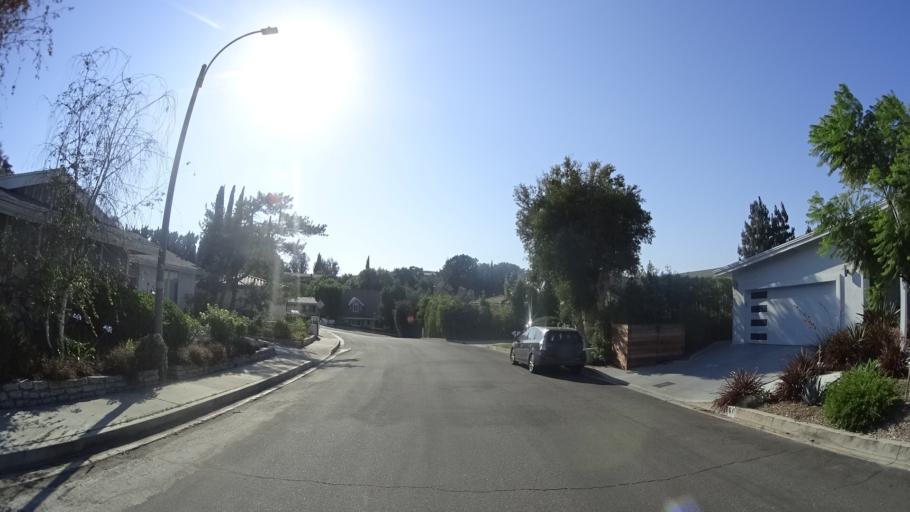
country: US
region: California
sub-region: Los Angeles County
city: Universal City
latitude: 34.1268
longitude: -118.3867
